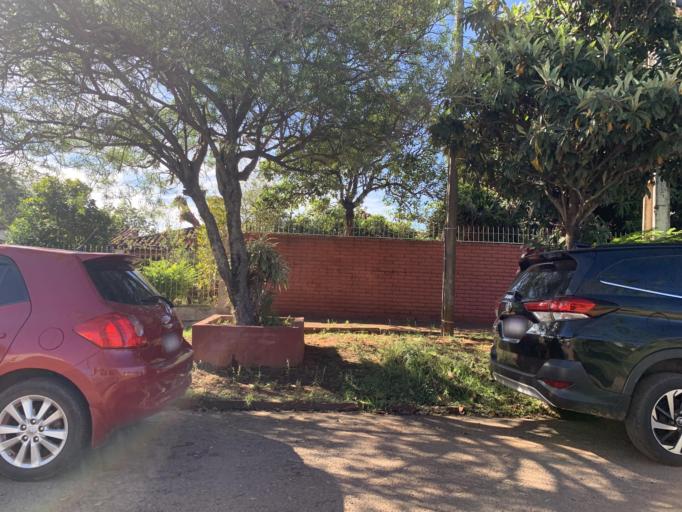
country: PY
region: Misiones
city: San Juan Bautista
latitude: -26.6706
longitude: -57.1382
